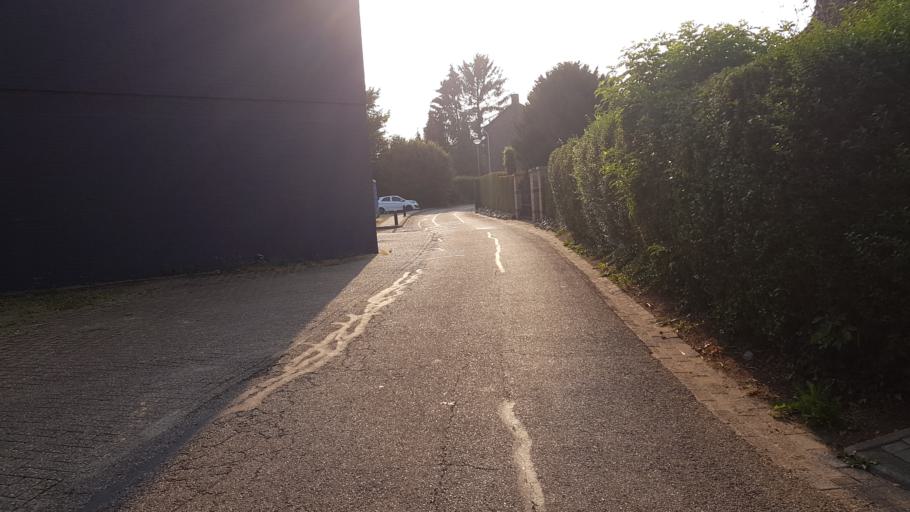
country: NL
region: Limburg
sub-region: Gemeente Beek
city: Beek
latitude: 50.9373
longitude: 5.7891
